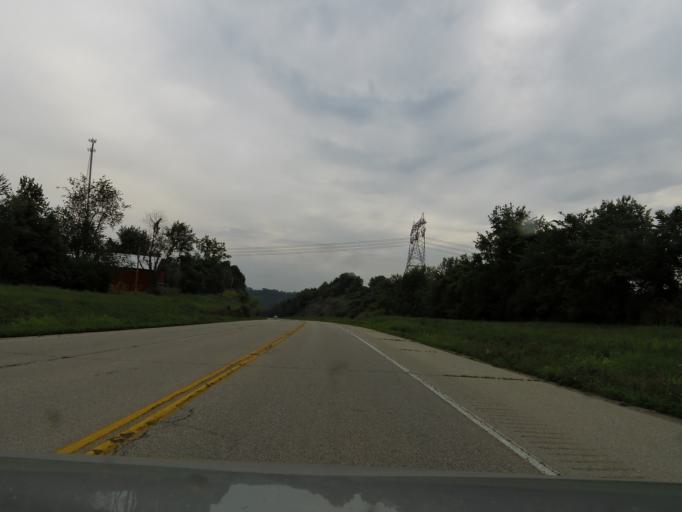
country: US
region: Ohio
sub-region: Brown County
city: Aberdeen
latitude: 38.5802
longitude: -83.8289
